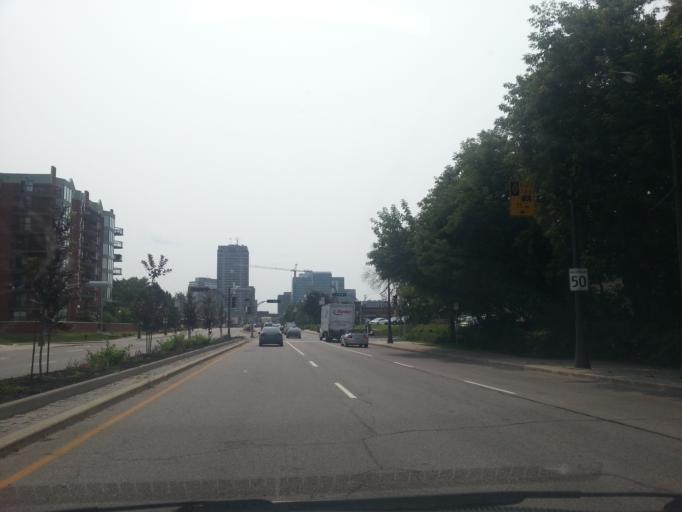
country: CA
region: Ontario
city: Ottawa
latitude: 45.4356
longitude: -75.7124
